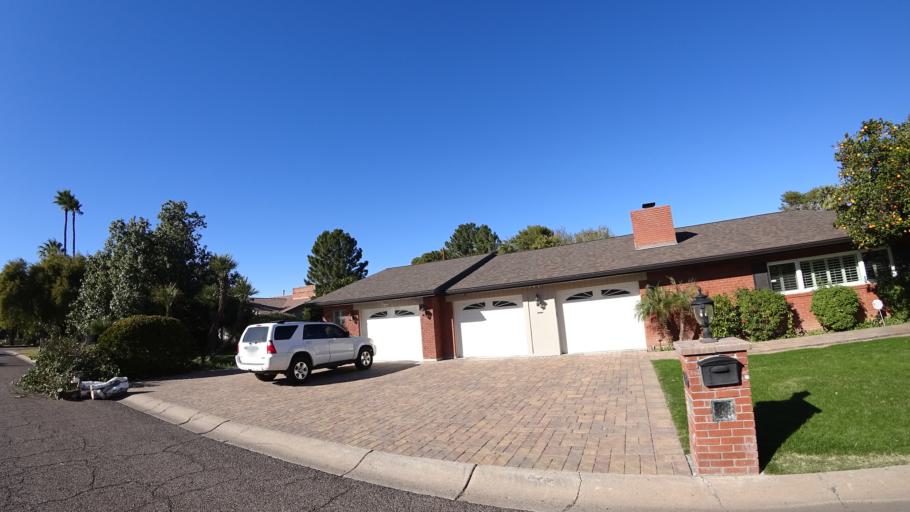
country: US
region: Arizona
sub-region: Maricopa County
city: Phoenix
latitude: 33.5505
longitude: -112.0709
